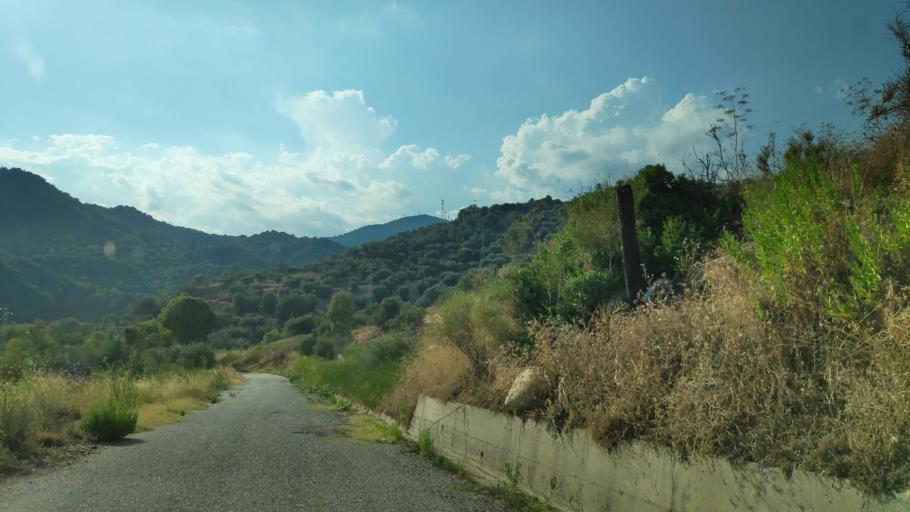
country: IT
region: Calabria
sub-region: Provincia di Reggio Calabria
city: Placanica
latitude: 38.4137
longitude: 16.4435
